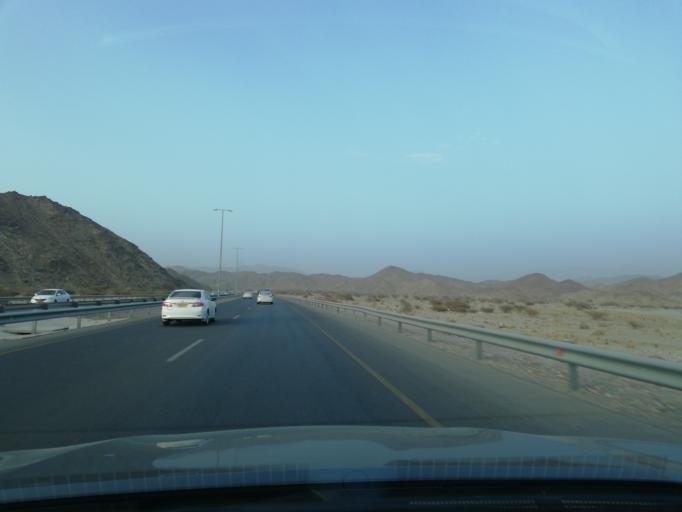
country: OM
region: Muhafazat ad Dakhiliyah
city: Bidbid
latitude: 23.3947
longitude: 58.0697
